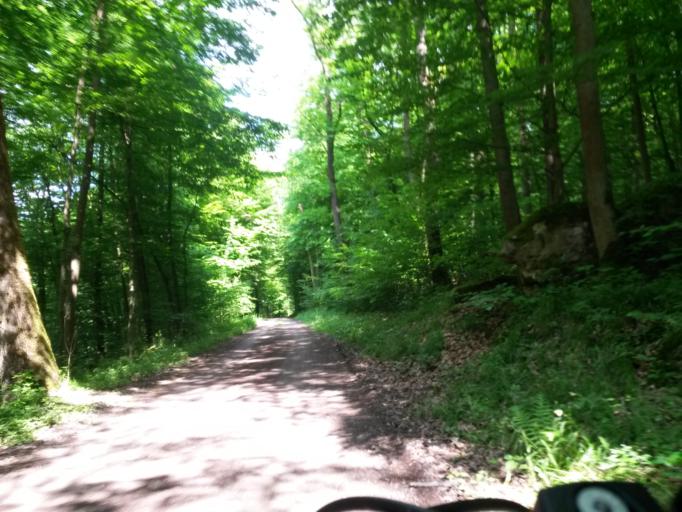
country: DE
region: Bavaria
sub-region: Regierungsbezirk Unterfranken
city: Euerdorf
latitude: 50.1678
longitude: 10.0474
